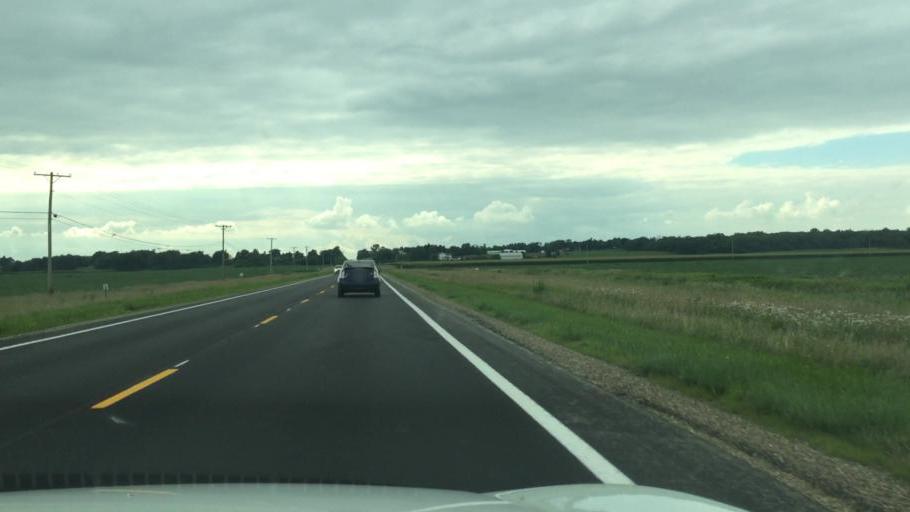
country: US
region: Ohio
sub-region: Champaign County
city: Mechanicsburg
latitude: 40.0806
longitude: -83.6482
